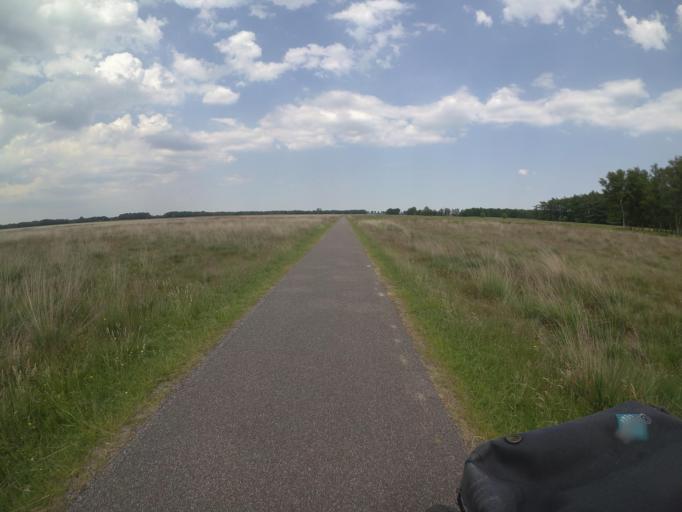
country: NL
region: Drenthe
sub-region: Gemeente Assen
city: Assen
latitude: 52.9171
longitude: 6.4999
